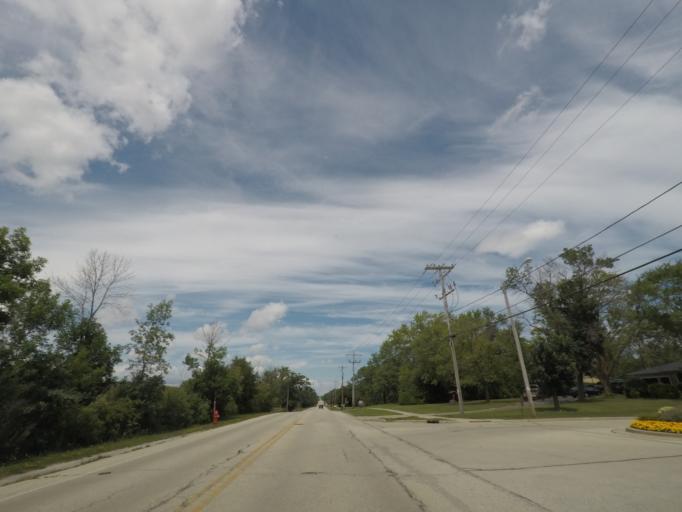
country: US
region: Wisconsin
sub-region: Milwaukee County
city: Greendale
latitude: 42.9057
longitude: -87.9799
